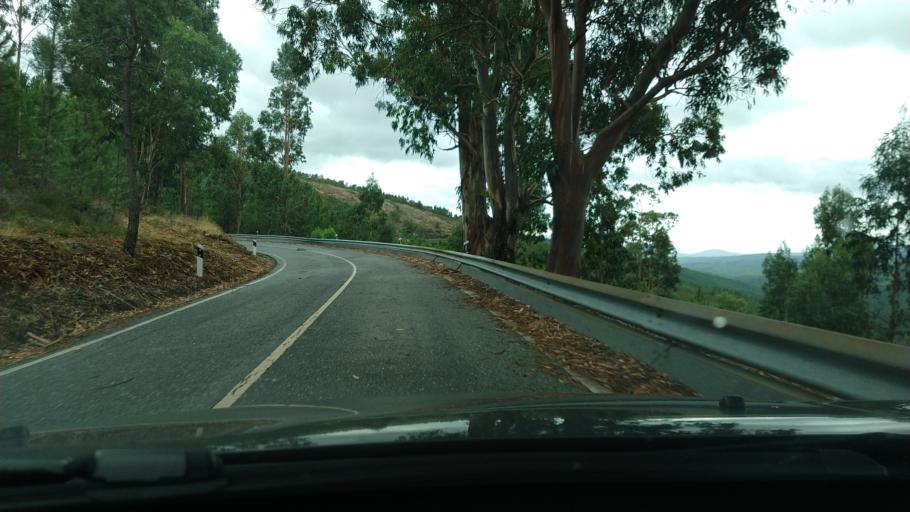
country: PT
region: Guarda
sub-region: Seia
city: Seia
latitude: 40.2437
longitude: -7.6756
